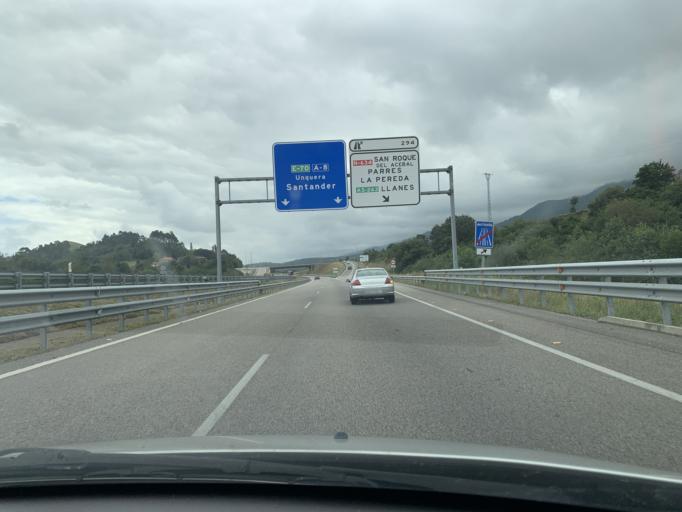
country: ES
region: Asturias
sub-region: Province of Asturias
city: Llanes
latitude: 43.4068
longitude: -4.7651
